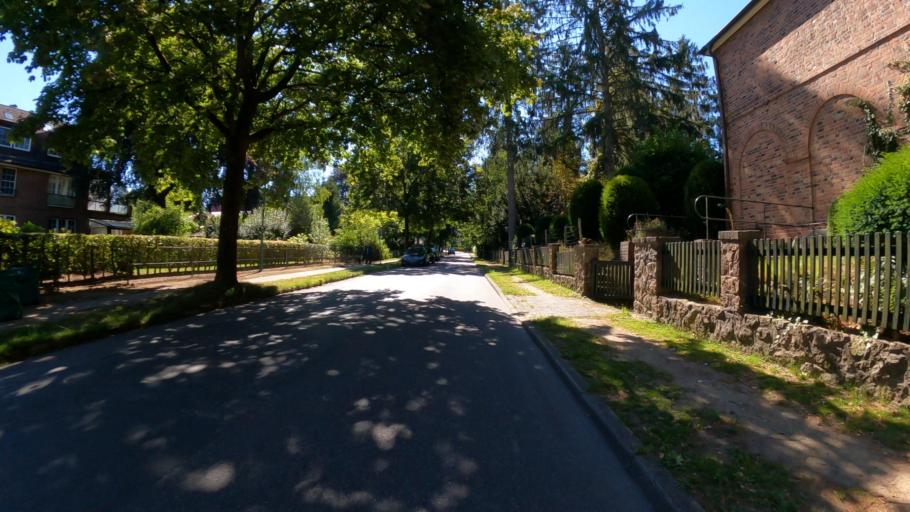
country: DE
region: Schleswig-Holstein
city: Aumuhle
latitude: 53.5262
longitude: 10.3139
